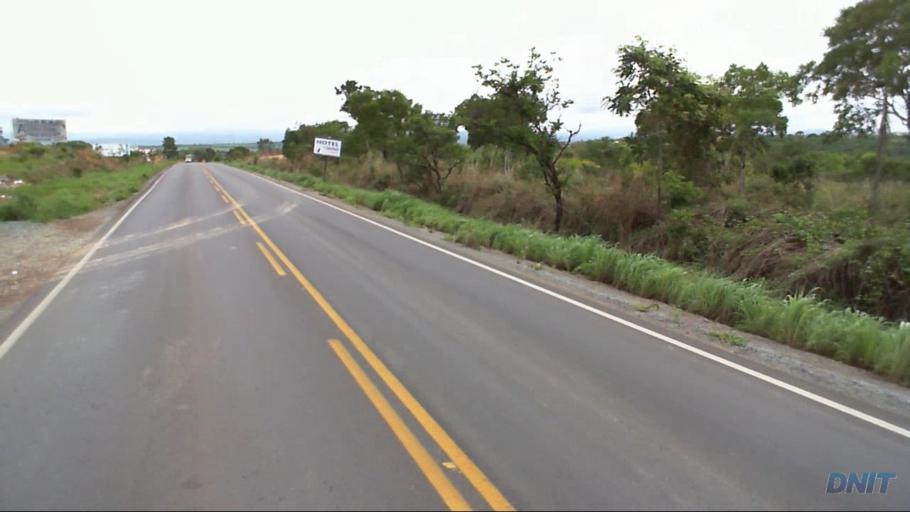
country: BR
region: Goias
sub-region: Padre Bernardo
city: Padre Bernardo
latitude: -15.1858
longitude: -48.2845
